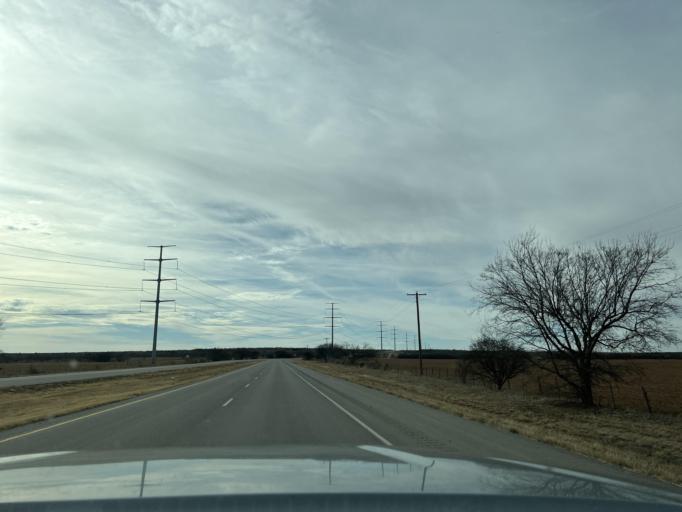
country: US
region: Texas
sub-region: Jones County
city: Stamford
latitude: 32.7517
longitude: -99.6263
